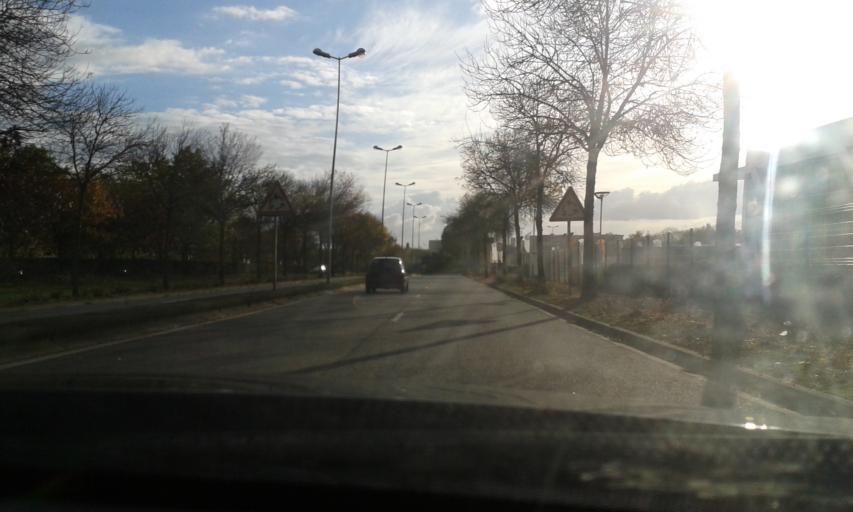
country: FR
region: Centre
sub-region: Departement d'Eure-et-Loir
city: Dreux
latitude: 48.7399
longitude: 1.3442
